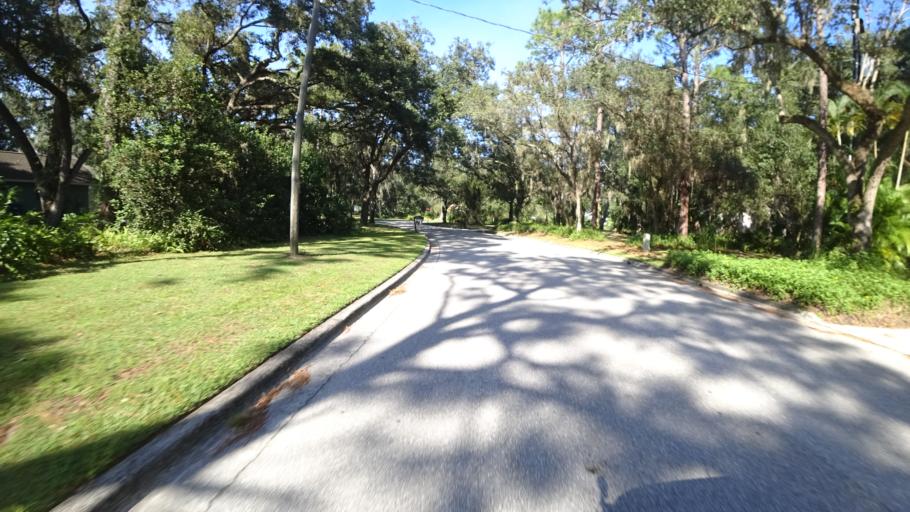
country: US
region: Florida
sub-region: Sarasota County
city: The Meadows
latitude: 27.4237
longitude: -82.4485
